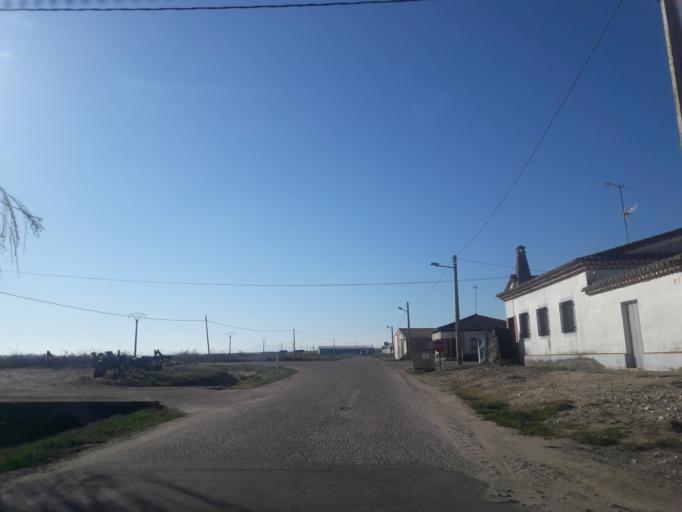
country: ES
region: Castille and Leon
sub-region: Provincia de Salamanca
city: Penarandilla
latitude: 40.8804
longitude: -5.3916
